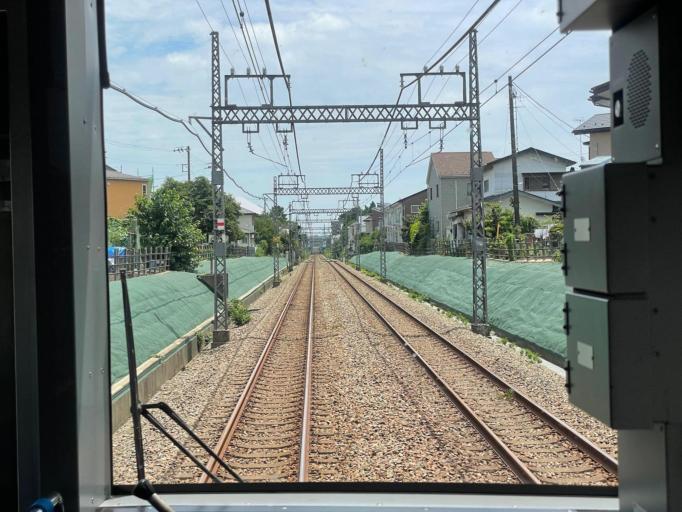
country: JP
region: Kanagawa
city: Fujisawa
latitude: 35.3915
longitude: 139.4682
